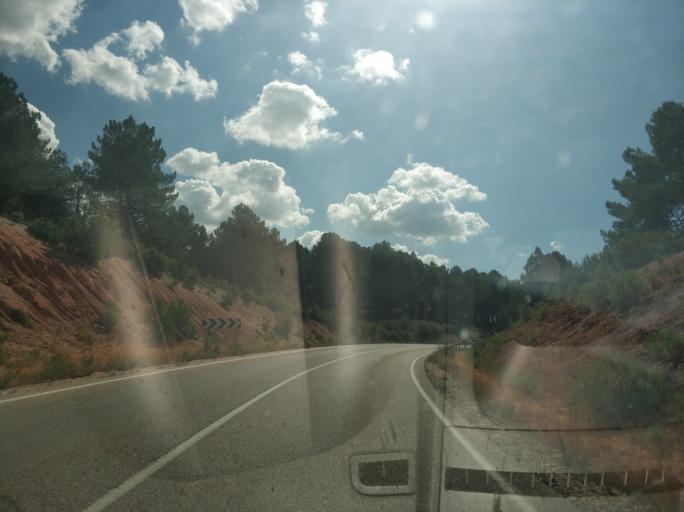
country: ES
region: Castille and Leon
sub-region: Provincia de Soria
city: Herrera de Soria
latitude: 41.7519
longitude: -3.0390
